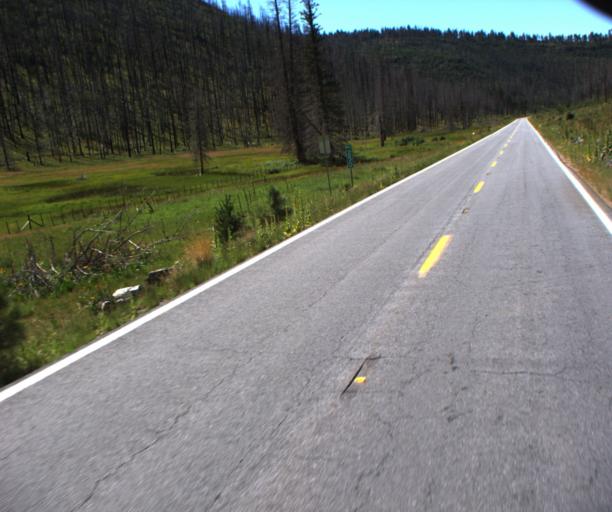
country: US
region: Arizona
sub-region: Apache County
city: Eagar
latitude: 33.8023
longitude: -109.1544
